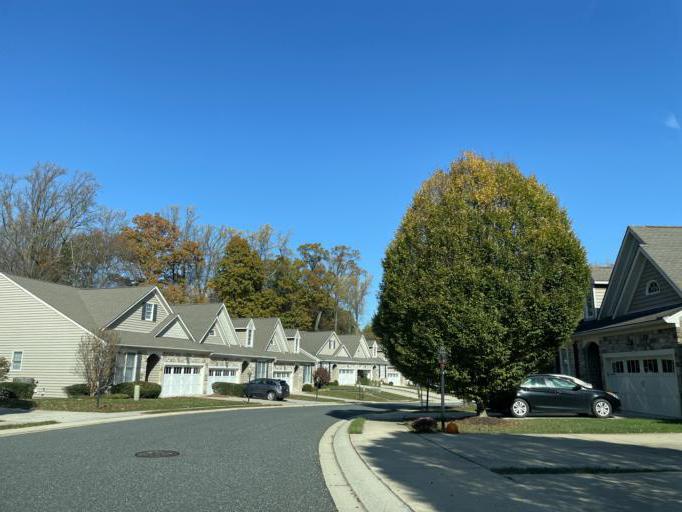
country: US
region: Maryland
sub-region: Harford County
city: Bel Air South
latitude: 39.4899
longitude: -76.3162
